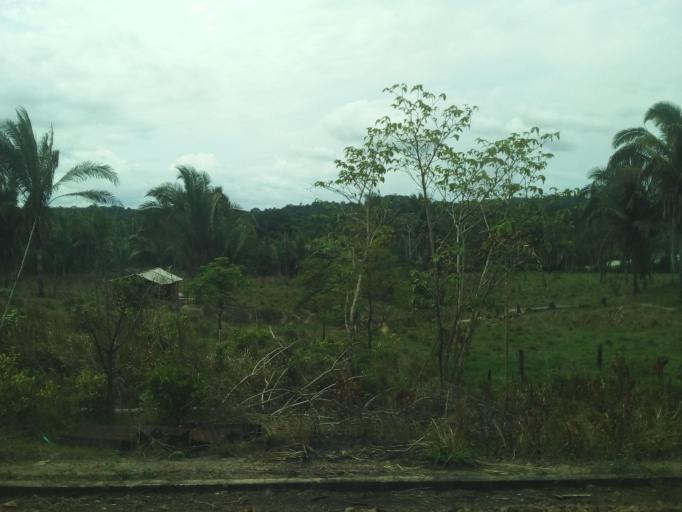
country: BR
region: Maranhao
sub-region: Santa Ines
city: Santa Ines
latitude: -3.7554
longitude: -46.1297
